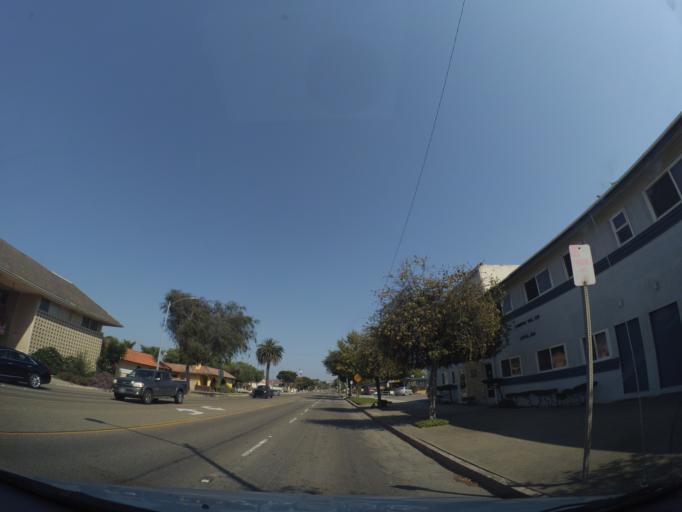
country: US
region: California
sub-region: Santa Barbara County
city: Lompoc
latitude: 34.6389
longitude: -120.4514
